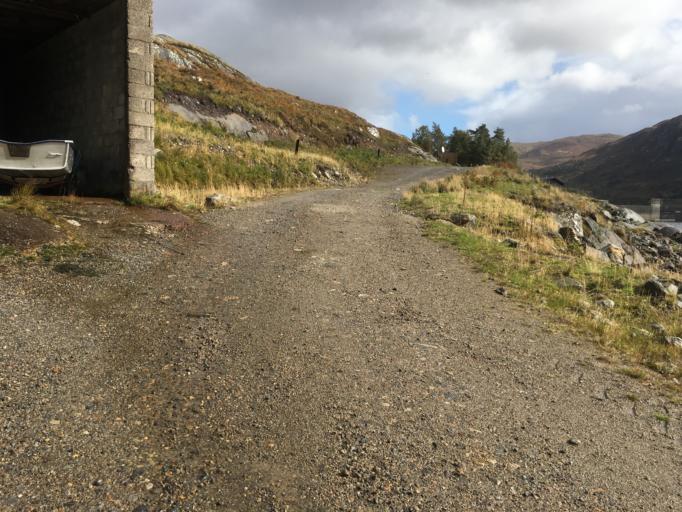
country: GB
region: Scotland
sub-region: Highland
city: Spean Bridge
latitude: 57.3398
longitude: -4.9635
